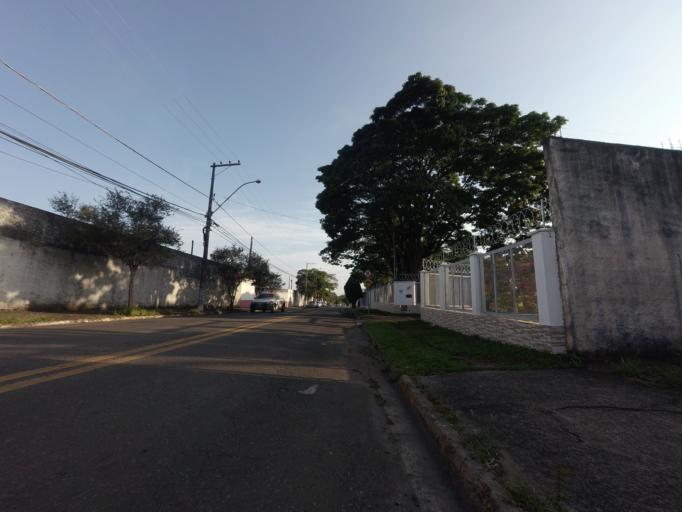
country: BR
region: Sao Paulo
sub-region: Piracicaba
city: Piracicaba
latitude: -22.7369
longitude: -47.6088
